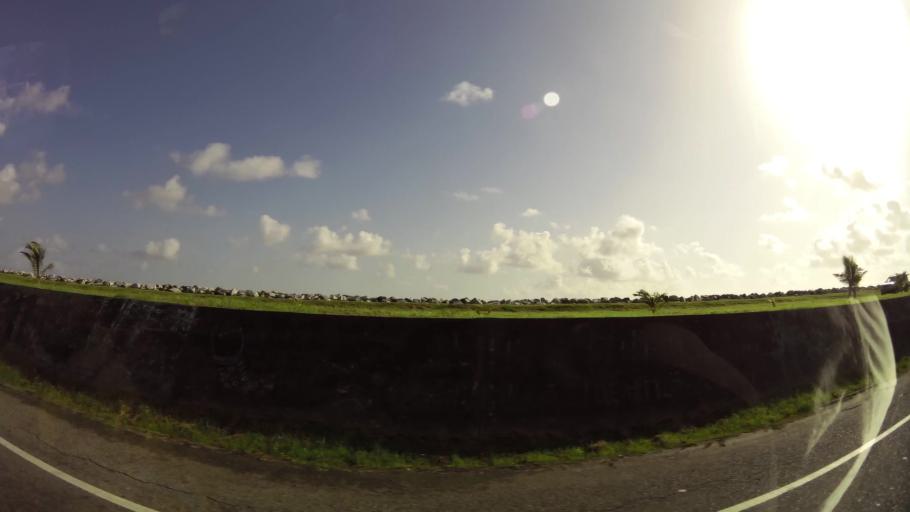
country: GY
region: Demerara-Mahaica
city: Georgetown
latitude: 6.8238
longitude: -58.1069
